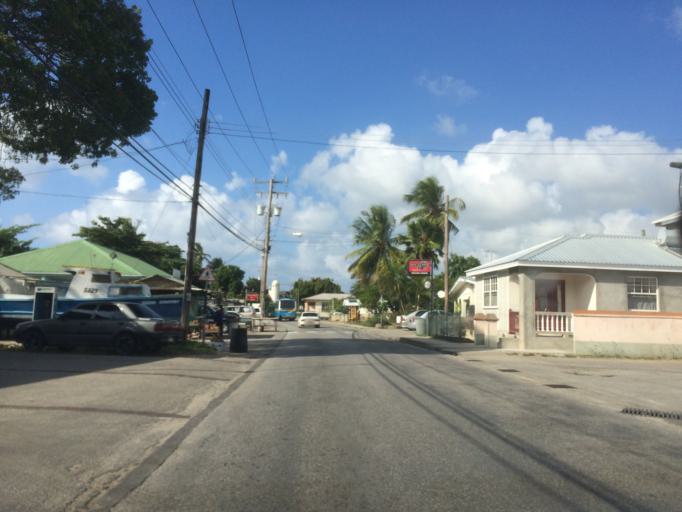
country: BB
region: Saint James
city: Holetown
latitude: 13.2167
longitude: -59.6412
